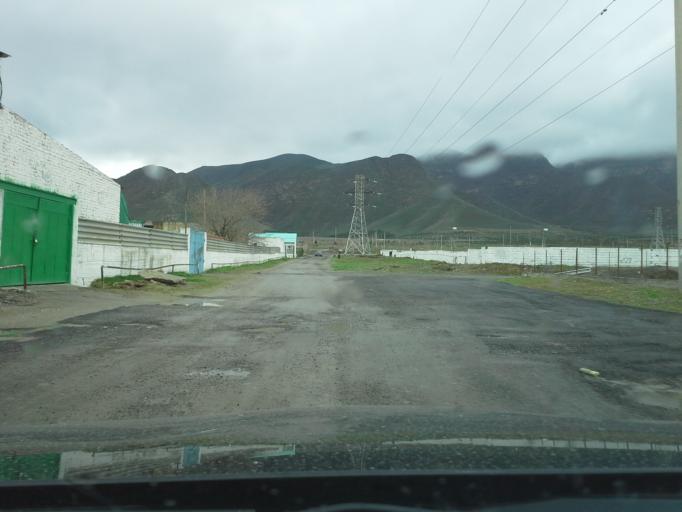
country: TM
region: Ahal
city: Abadan
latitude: 37.9504
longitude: 58.2056
